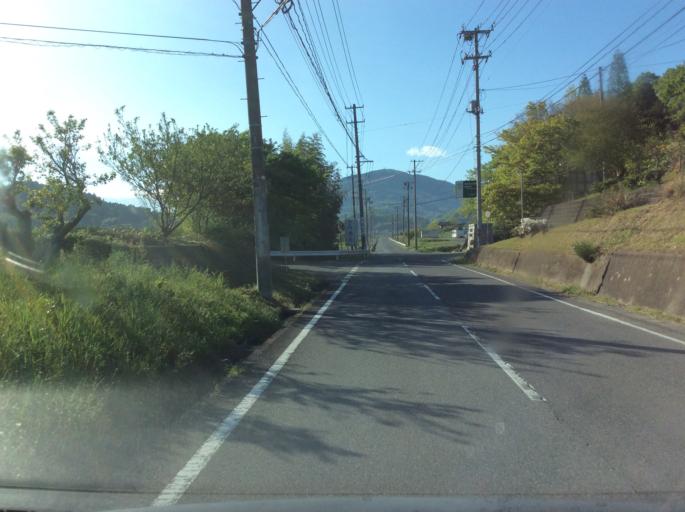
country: JP
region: Fukushima
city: Iwaki
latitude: 36.9877
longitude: 140.8313
